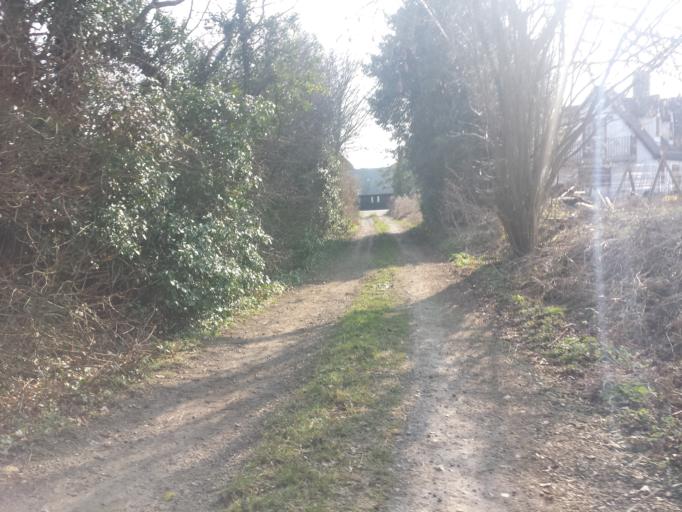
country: GB
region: England
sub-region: Essex
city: Little Clacton
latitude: 51.8871
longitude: 1.1614
